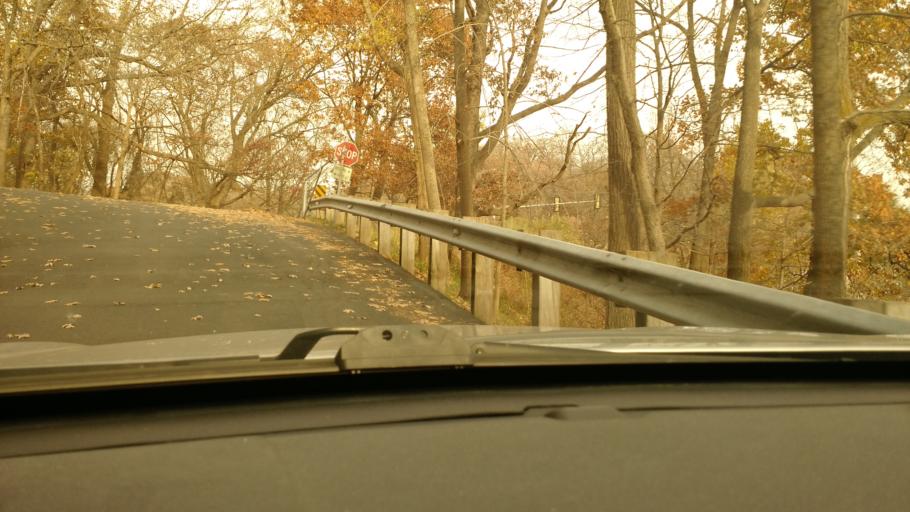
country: US
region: Illinois
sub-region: Rock Island County
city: Milan
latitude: 41.4646
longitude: -90.5666
